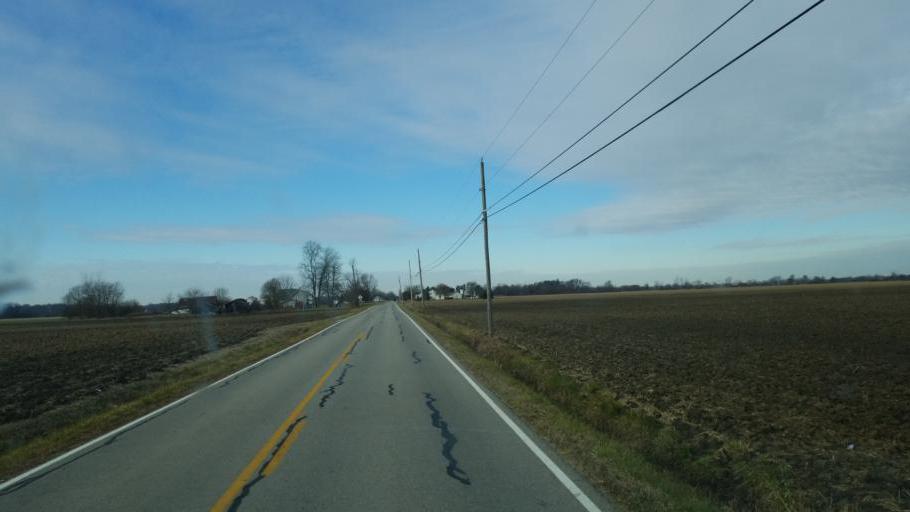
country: US
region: Ohio
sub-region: Marion County
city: Marion
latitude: 40.5643
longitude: -83.0203
